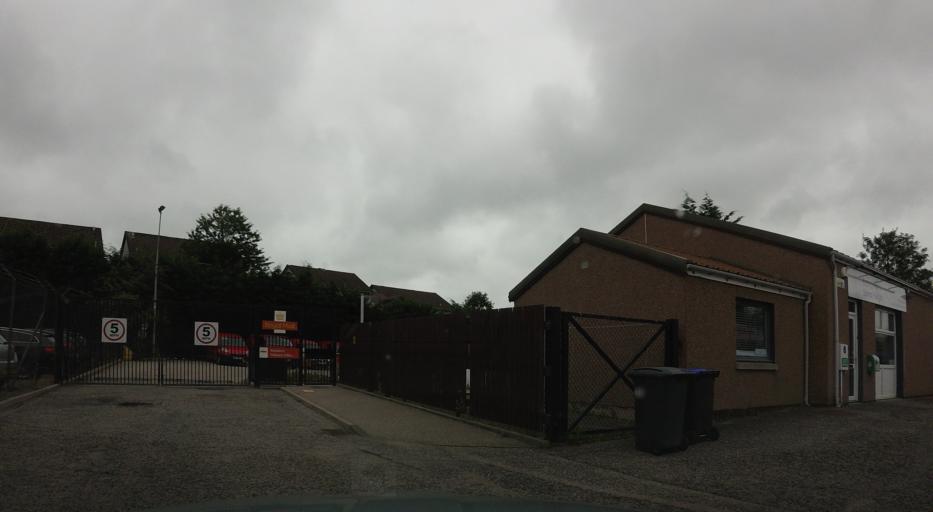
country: GB
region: Scotland
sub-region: Aberdeenshire
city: Banchory
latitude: 57.0569
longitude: -2.4862
